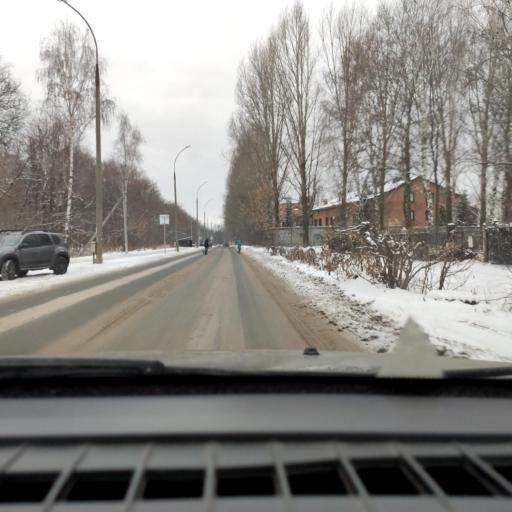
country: RU
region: Samara
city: Tol'yatti
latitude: 53.5050
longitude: 49.3052
